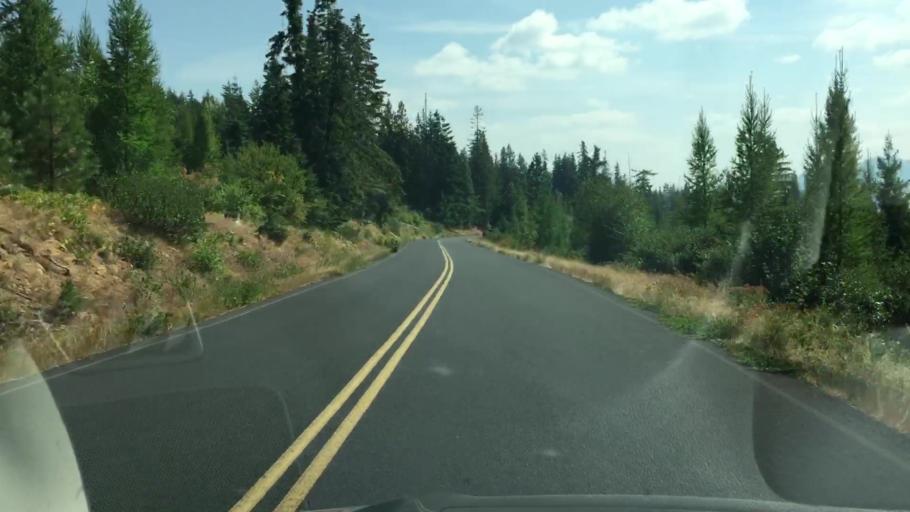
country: US
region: Washington
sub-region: Klickitat County
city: White Salmon
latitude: 46.0336
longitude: -121.5446
